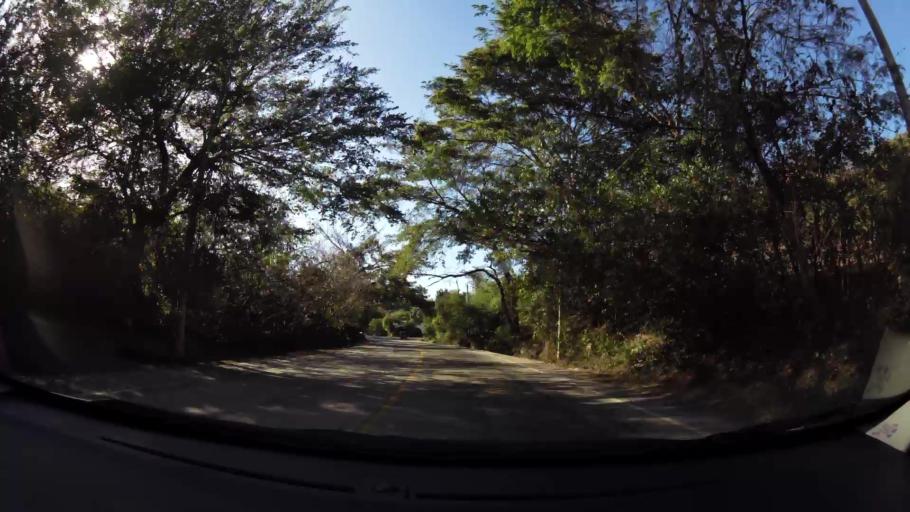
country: SV
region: Santa Ana
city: Texistepeque
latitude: 14.1381
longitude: -89.5093
